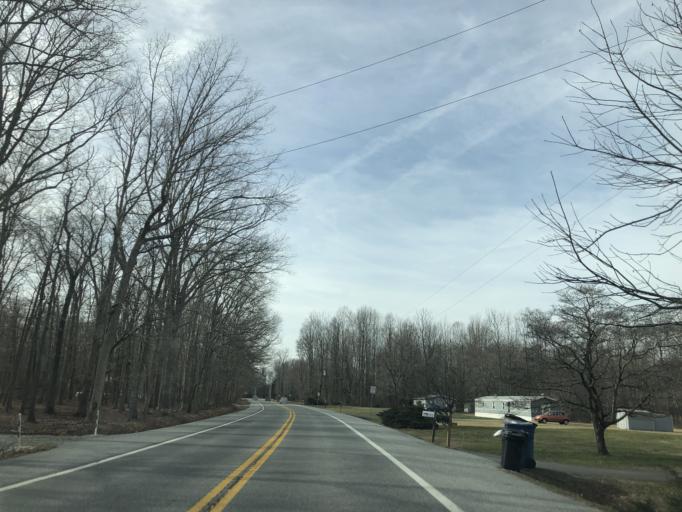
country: US
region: Delaware
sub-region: Kent County
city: Smyrna
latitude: 39.2809
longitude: -75.5574
